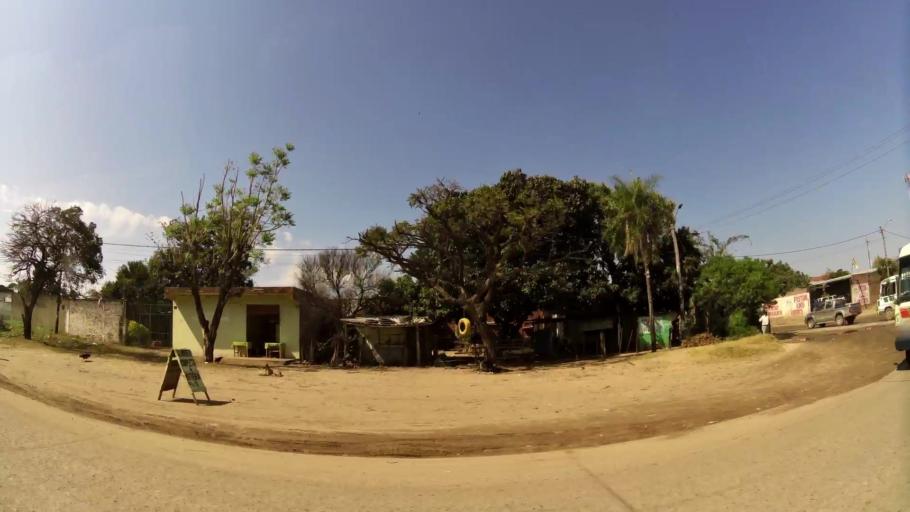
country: BO
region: Santa Cruz
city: Santa Cruz de la Sierra
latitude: -17.7539
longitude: -63.1206
